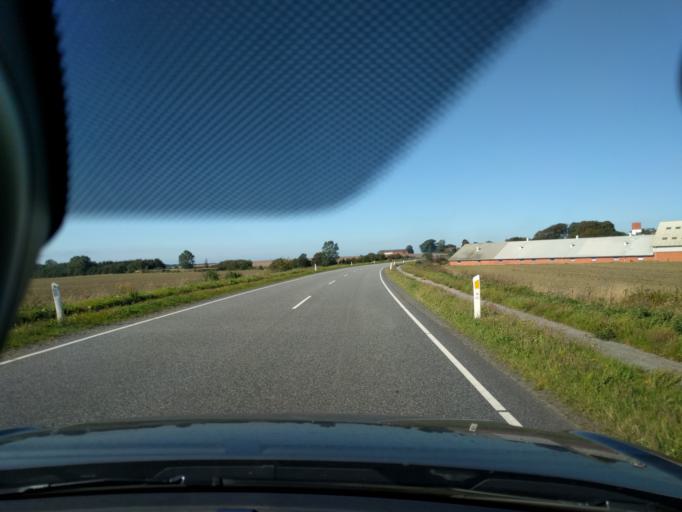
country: DK
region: North Denmark
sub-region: Vesthimmerland Kommune
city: Aars
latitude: 56.7463
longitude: 9.5909
